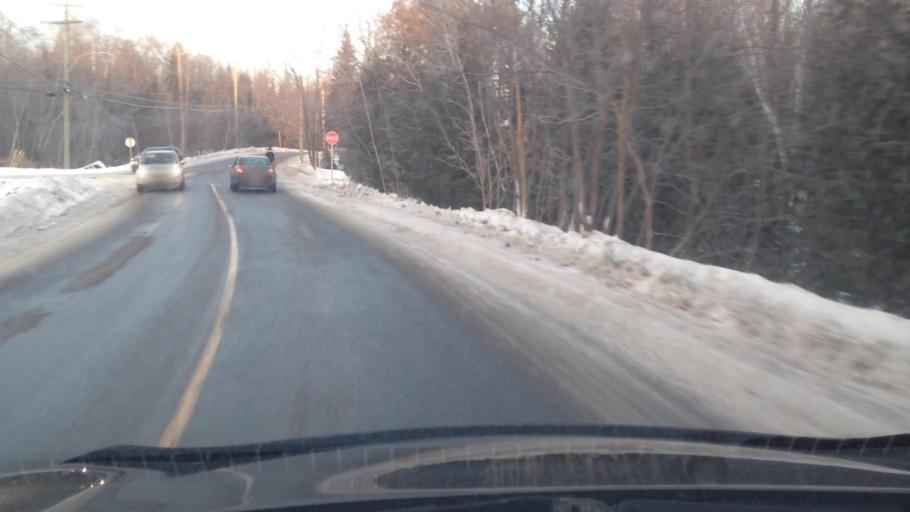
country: CA
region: Quebec
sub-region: Lanaudiere
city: Sainte-Julienne
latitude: 45.9524
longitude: -73.7411
